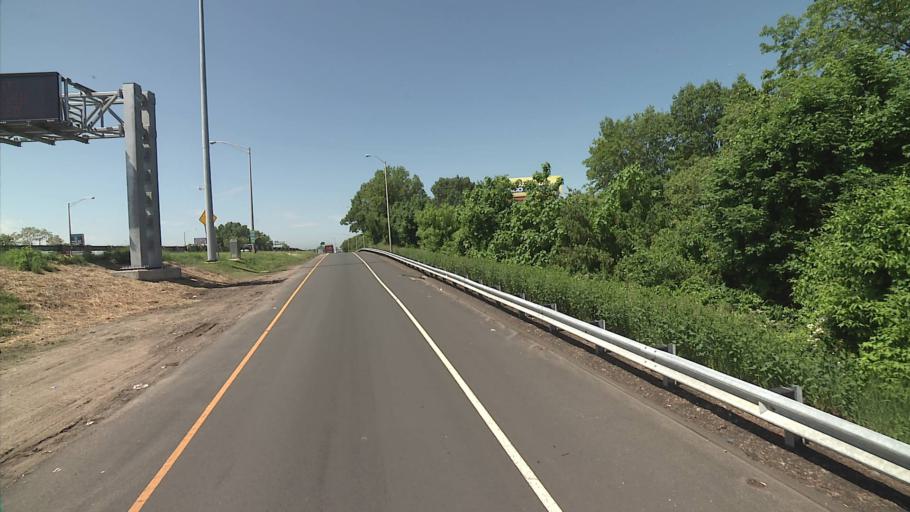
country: US
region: Connecticut
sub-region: Fairfield County
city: Stratford
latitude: 41.1822
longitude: -73.1439
